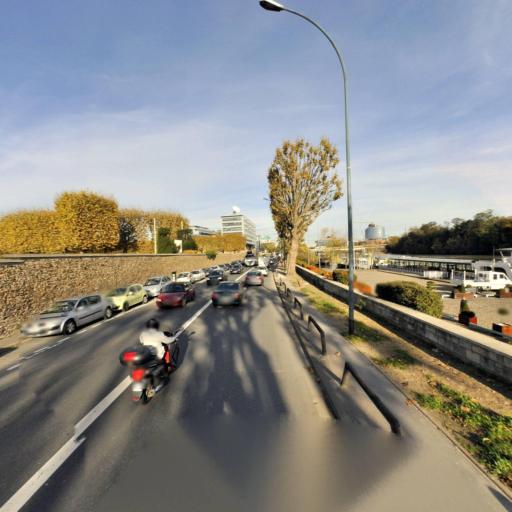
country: FR
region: Ile-de-France
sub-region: Departement des Hauts-de-Seine
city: Boulogne-Billancourt
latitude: 48.8287
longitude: 2.2545
